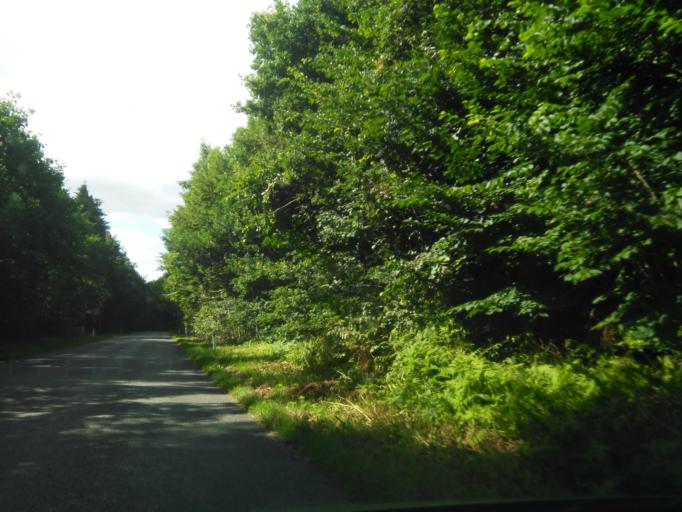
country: DK
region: Central Jutland
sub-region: Skanderborg Kommune
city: Horning
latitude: 56.1094
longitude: 10.0186
